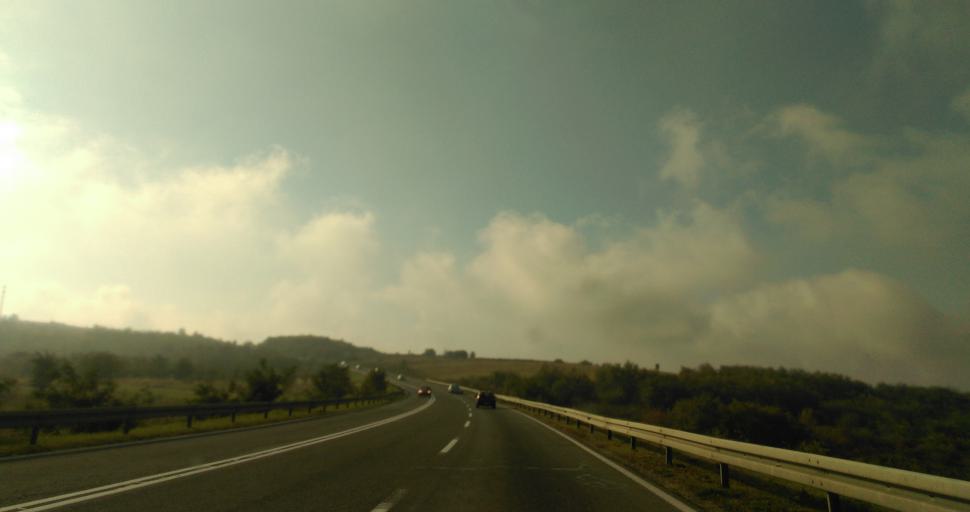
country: RS
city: Rusanj
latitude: 44.6677
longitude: 20.4255
